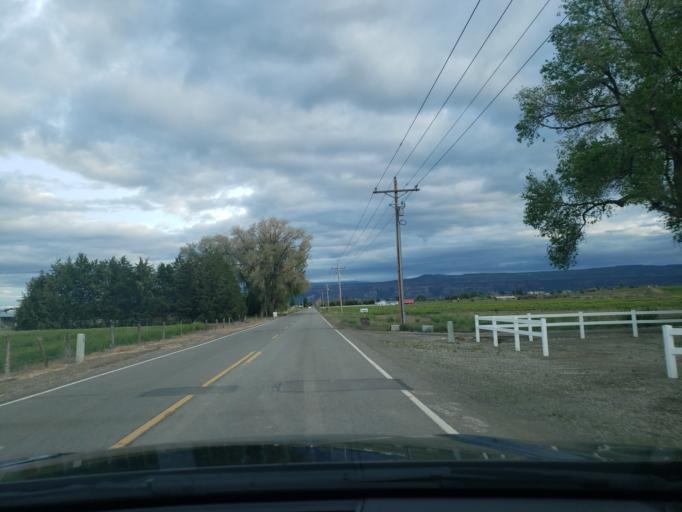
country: US
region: Colorado
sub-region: Mesa County
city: Fruita
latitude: 39.2188
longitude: -108.7011
